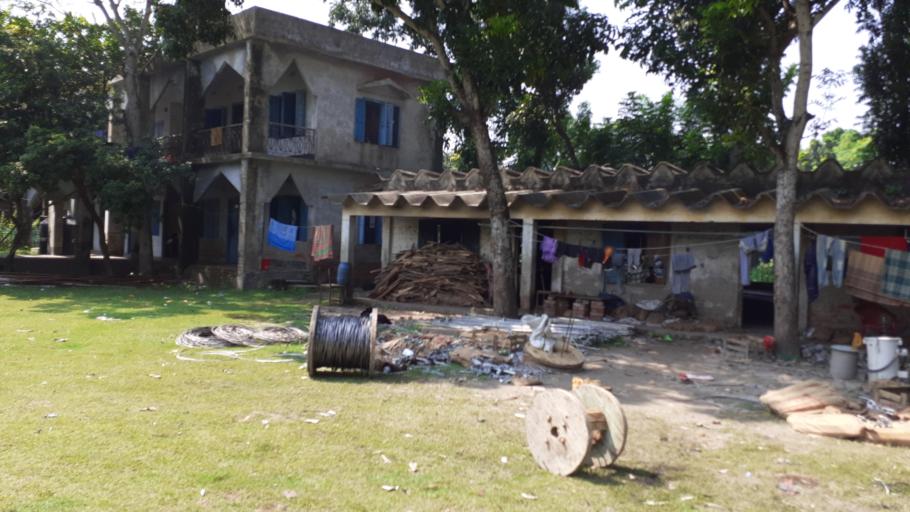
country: BD
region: Khulna
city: Phultala
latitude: 22.6417
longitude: 89.4214
